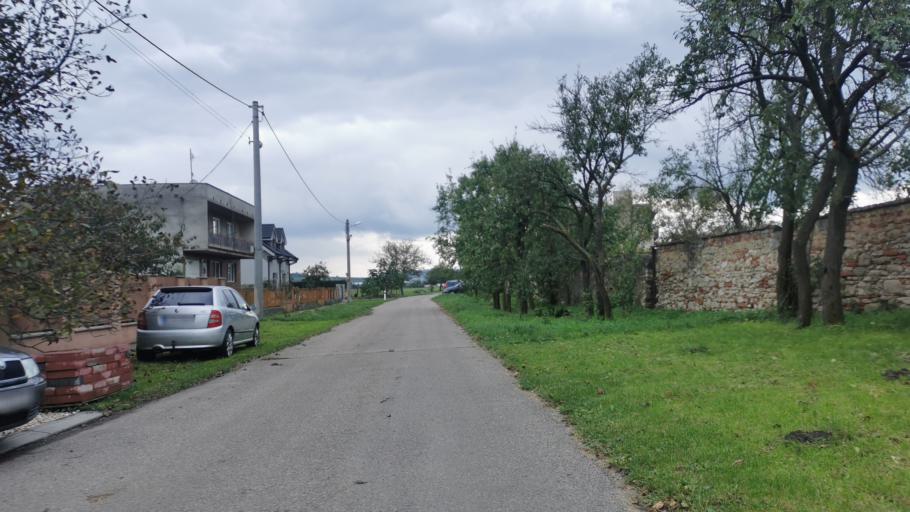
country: SK
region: Trnavsky
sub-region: Okres Skalica
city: Holic
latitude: 48.8241
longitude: 17.1934
